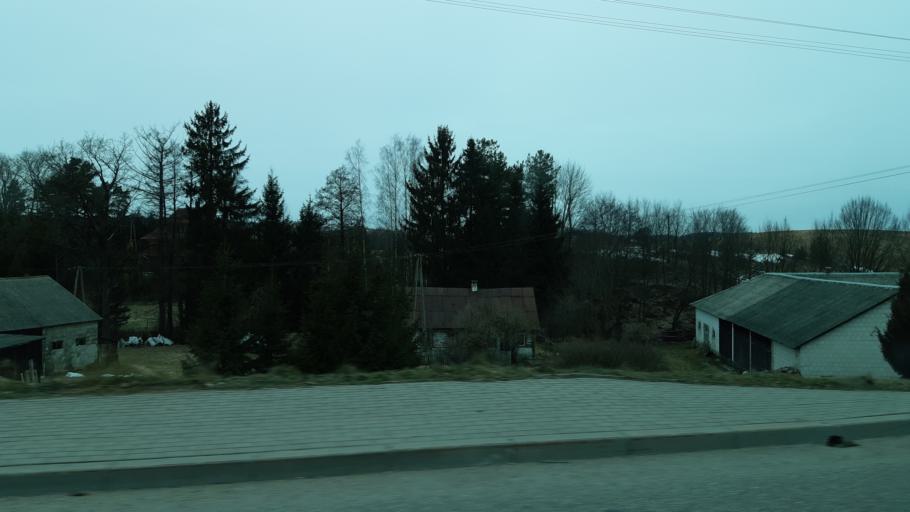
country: PL
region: Podlasie
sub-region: Suwalki
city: Suwalki
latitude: 54.3158
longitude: 22.9620
